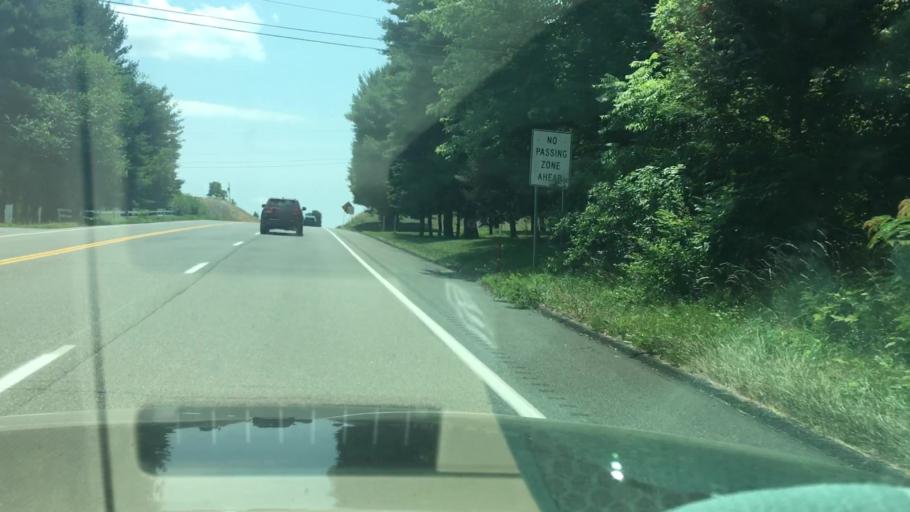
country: US
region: Pennsylvania
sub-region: Lehigh County
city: Schnecksville
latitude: 40.6516
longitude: -75.6847
